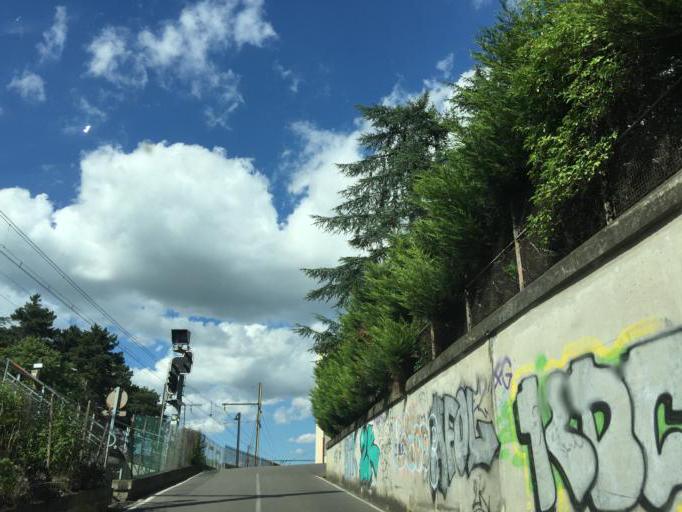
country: FR
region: Rhone-Alpes
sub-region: Departement de la Loire
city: Saint-Chamond
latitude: 45.4743
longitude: 4.5207
